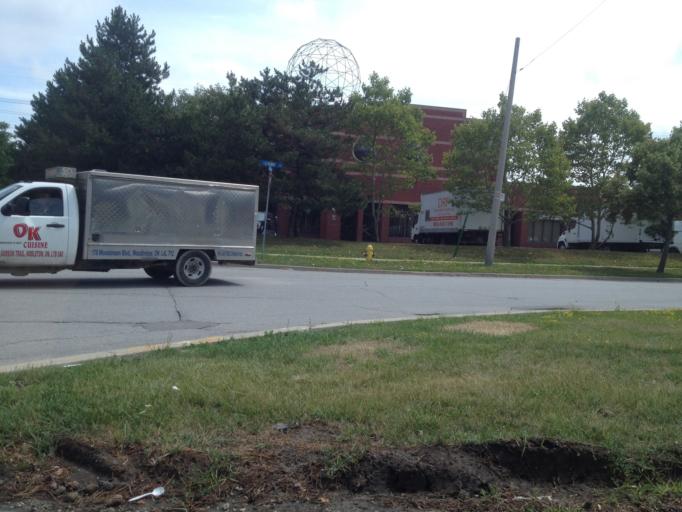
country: CA
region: Ontario
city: Etobicoke
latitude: 43.7535
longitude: -79.6091
